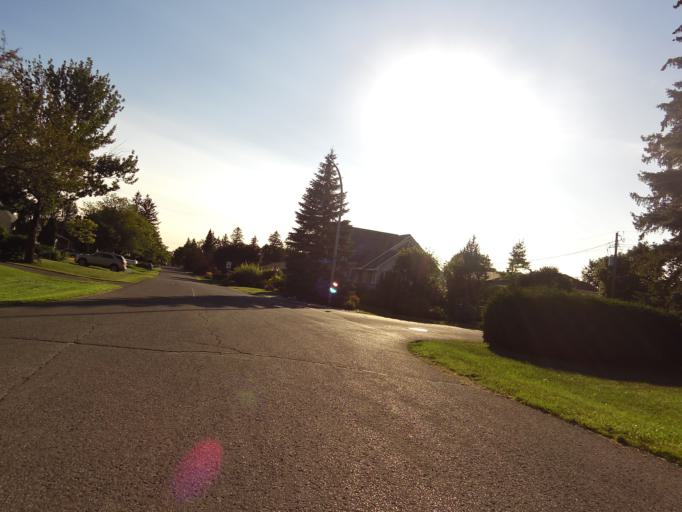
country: CA
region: Ontario
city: Ottawa
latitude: 45.3559
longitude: -75.7390
